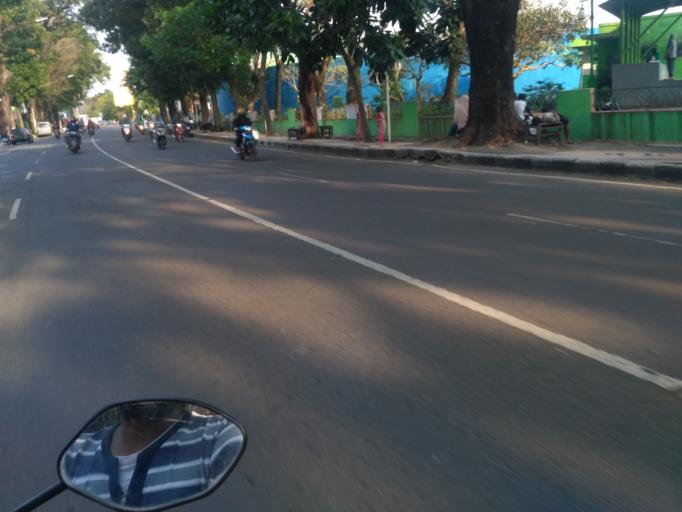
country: ID
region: East Java
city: Malang
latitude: -7.9742
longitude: 112.6251
